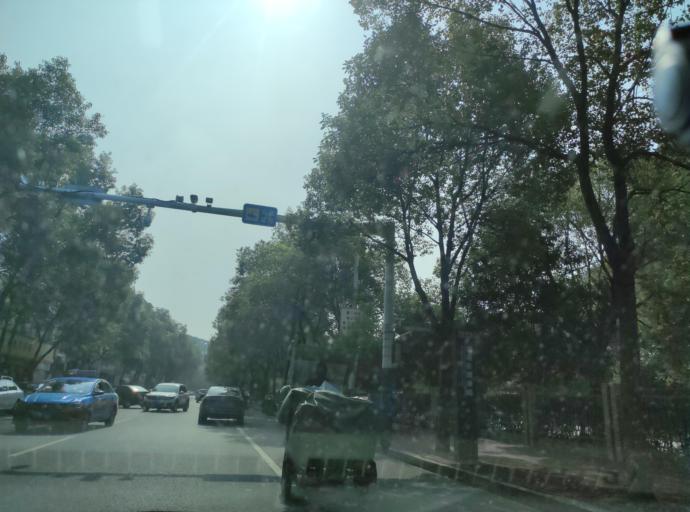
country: CN
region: Jiangxi Sheng
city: Pingxiang
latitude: 27.6434
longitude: 113.8551
